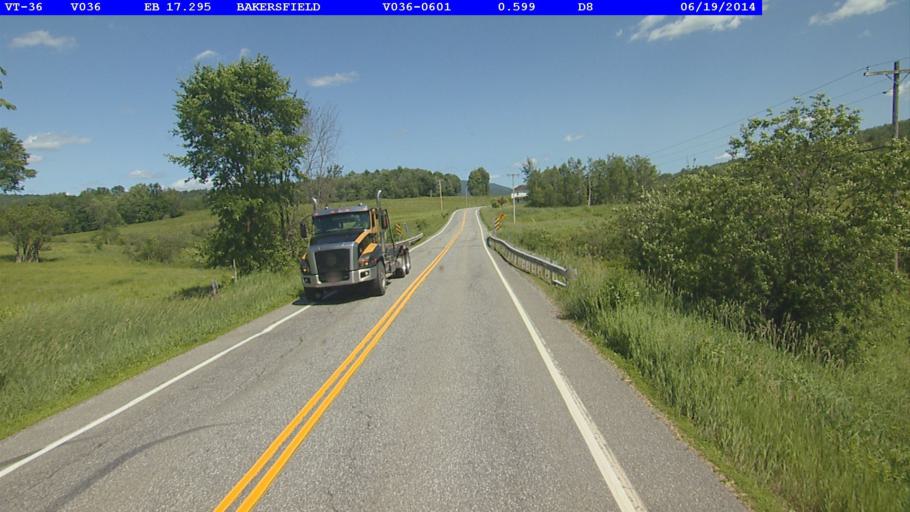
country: US
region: Vermont
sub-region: Franklin County
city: Enosburg Falls
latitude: 44.7847
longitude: -72.8378
